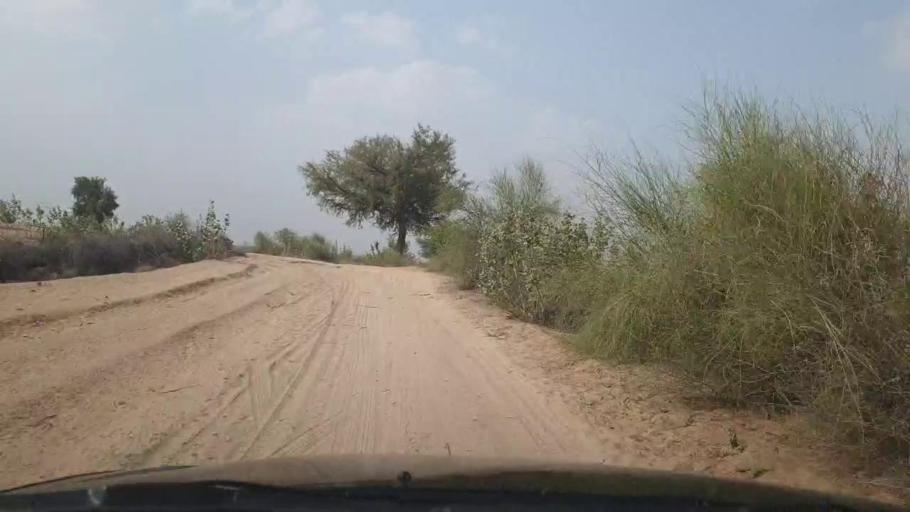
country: PK
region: Sindh
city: Islamkot
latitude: 24.9613
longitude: 70.6316
